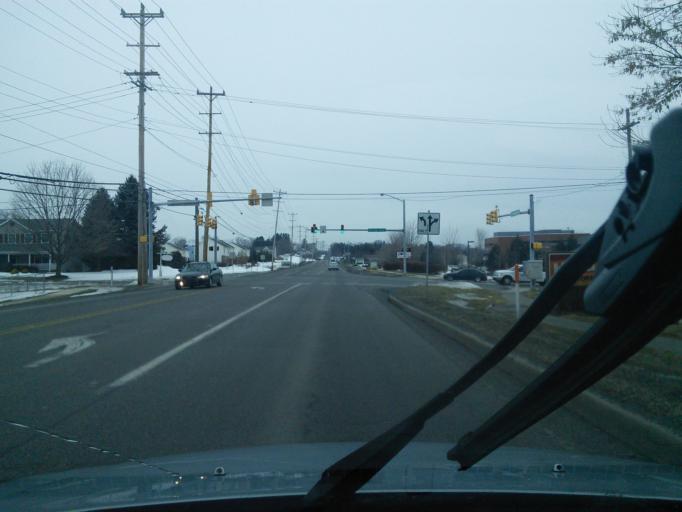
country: US
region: Pennsylvania
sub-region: Centre County
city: Pine Grove Mills
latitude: 40.7654
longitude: -77.8834
